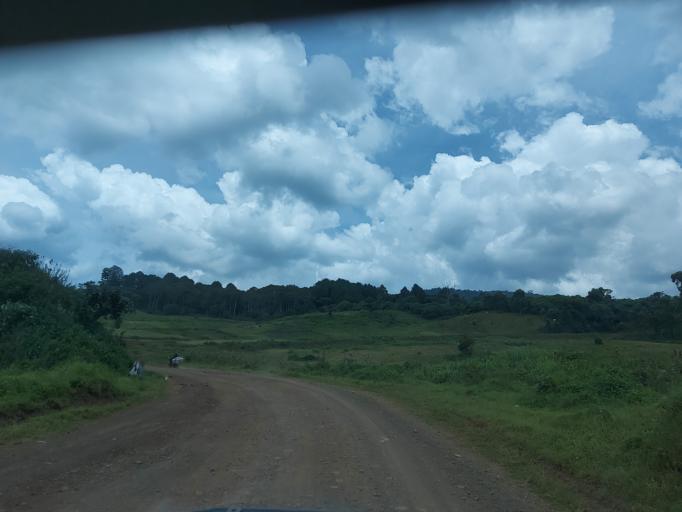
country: CD
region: South Kivu
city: Kabare
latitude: -2.3179
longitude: 28.7625
